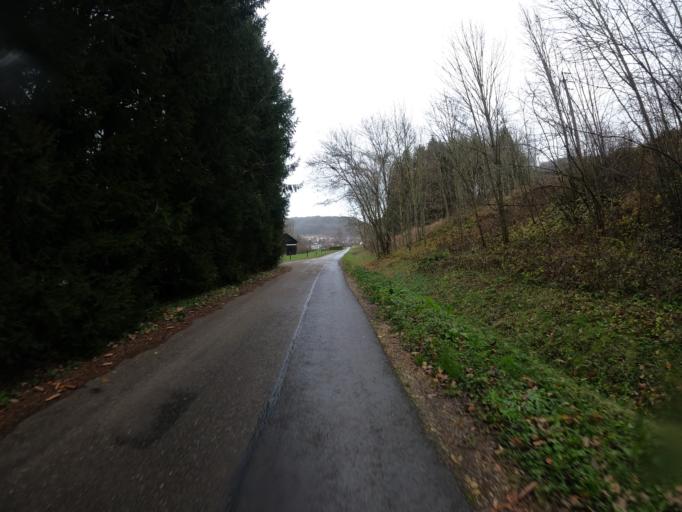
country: DE
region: Baden-Wuerttemberg
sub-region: Regierungsbezirk Stuttgart
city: Donzdorf
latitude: 48.7036
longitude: 9.8479
